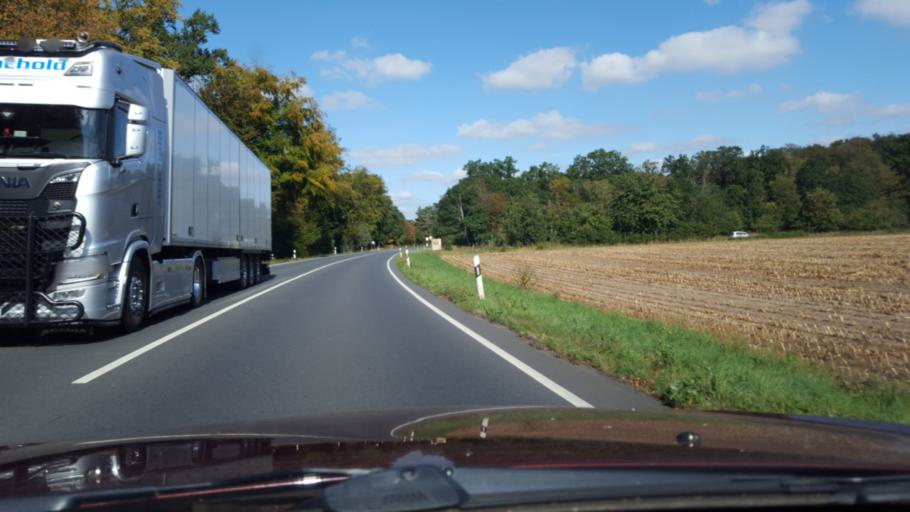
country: DE
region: Lower Saxony
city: Eystrup
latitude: 52.8153
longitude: 9.1991
